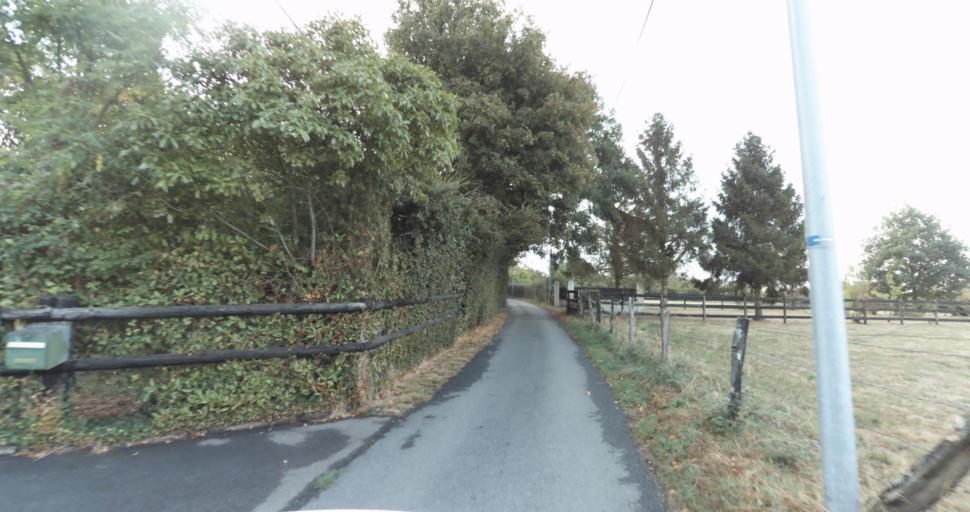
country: FR
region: Lower Normandy
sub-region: Departement de l'Orne
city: Vimoutiers
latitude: 48.9385
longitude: 0.2114
